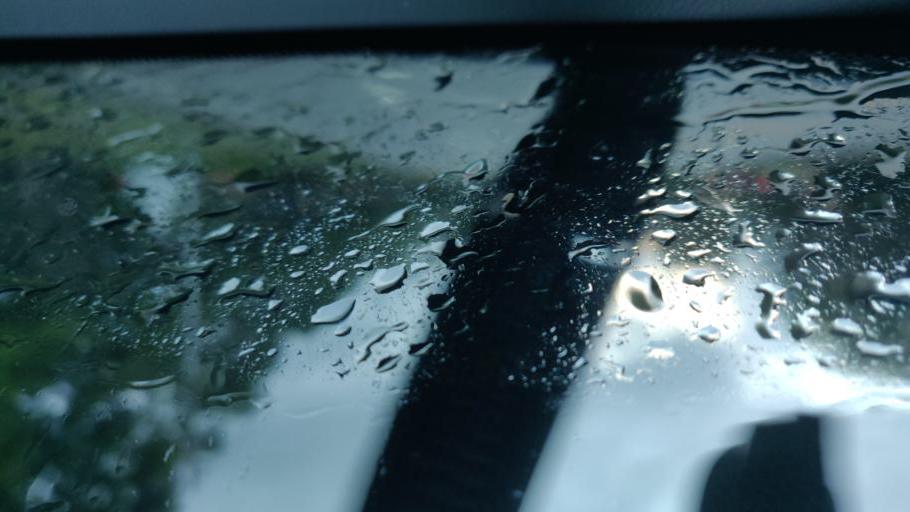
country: US
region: Florida
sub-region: Palm Beach County
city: Schall Circle
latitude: 26.7216
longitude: -80.1166
